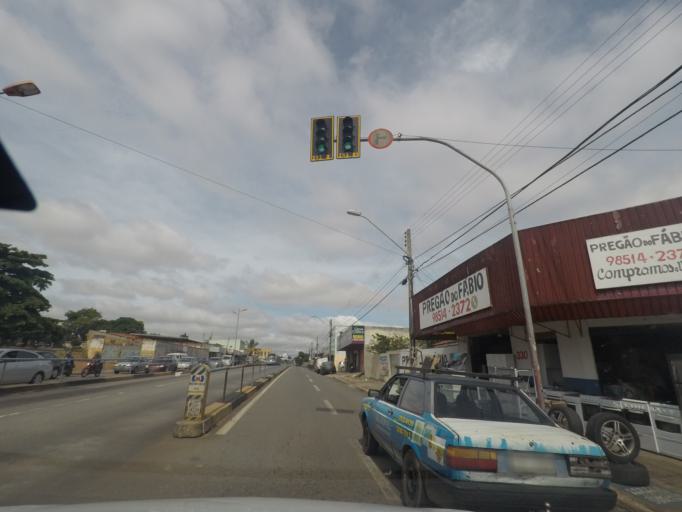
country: BR
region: Goias
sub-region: Goiania
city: Goiania
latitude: -16.6679
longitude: -49.2144
